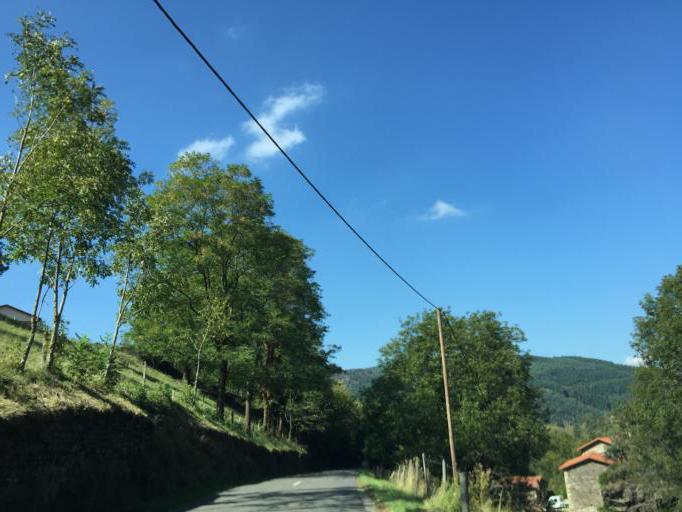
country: FR
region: Rhone-Alpes
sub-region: Departement de la Loire
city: Saint-Paul-en-Jarez
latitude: 45.4296
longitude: 4.5796
